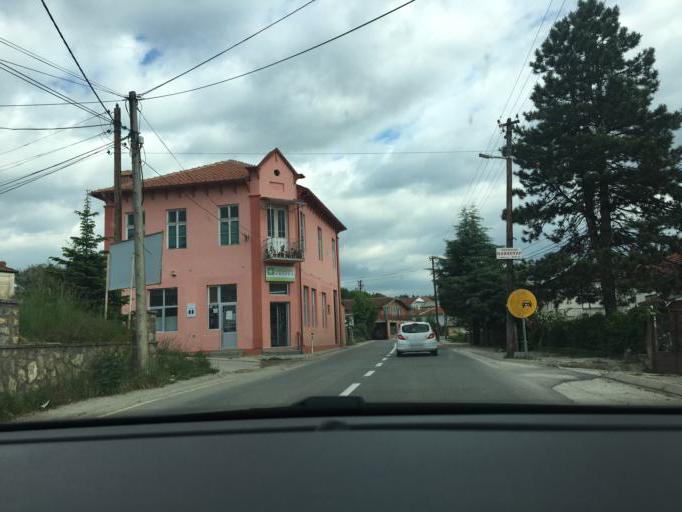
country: MK
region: Resen
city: Jankovec
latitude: 41.1083
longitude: 21.0117
